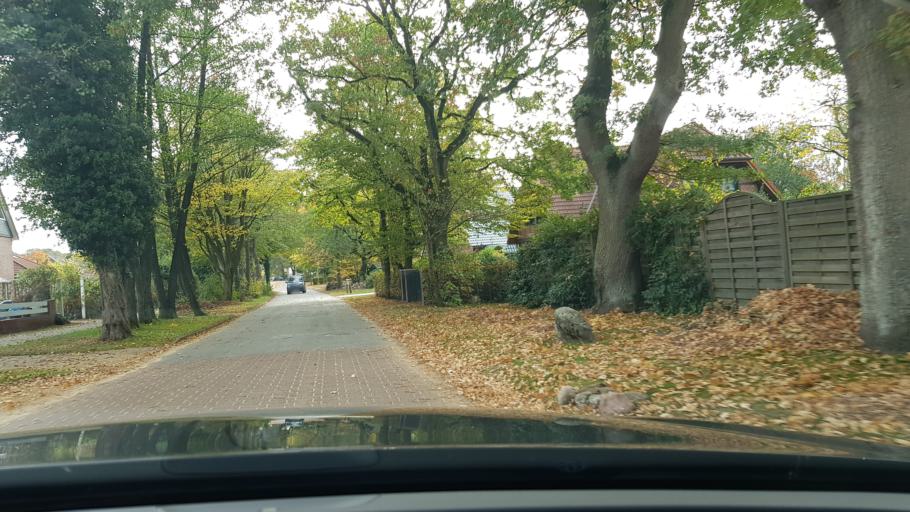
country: DE
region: Lower Saxony
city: Beverstedt
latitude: 53.4285
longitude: 8.8131
